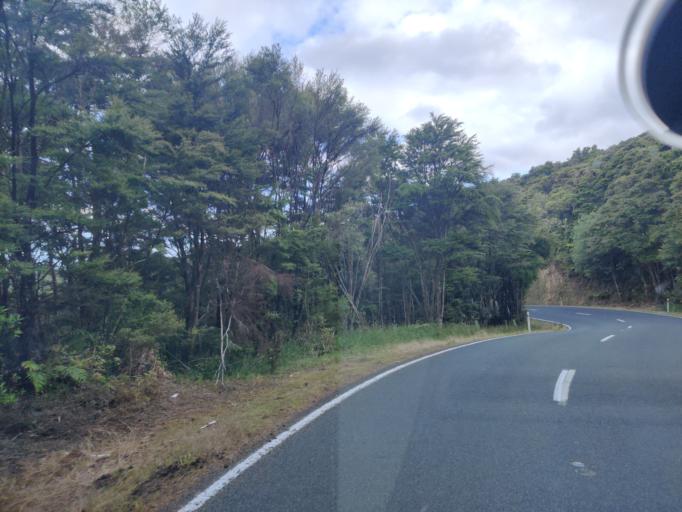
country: NZ
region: Northland
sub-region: Whangarei
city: Ngunguru
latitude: -35.5791
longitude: 174.4095
